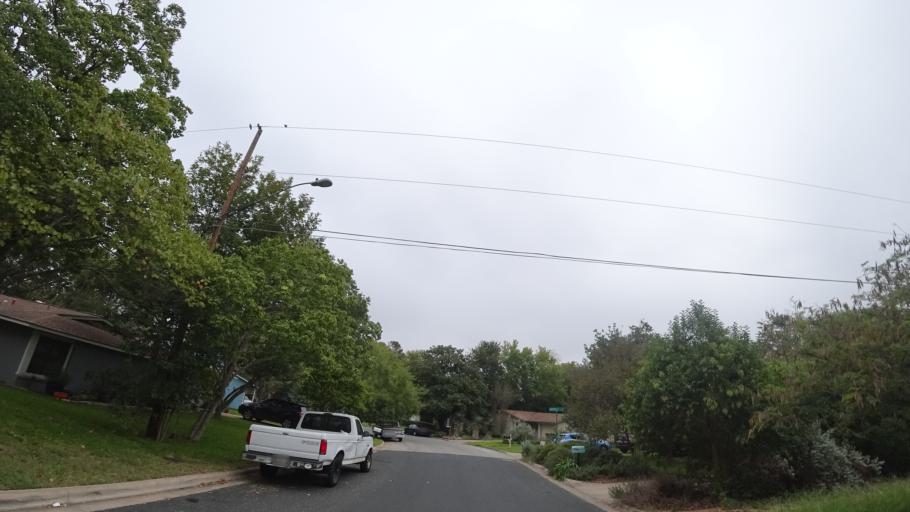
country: US
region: Texas
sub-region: Travis County
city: Austin
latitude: 30.2092
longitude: -97.7792
